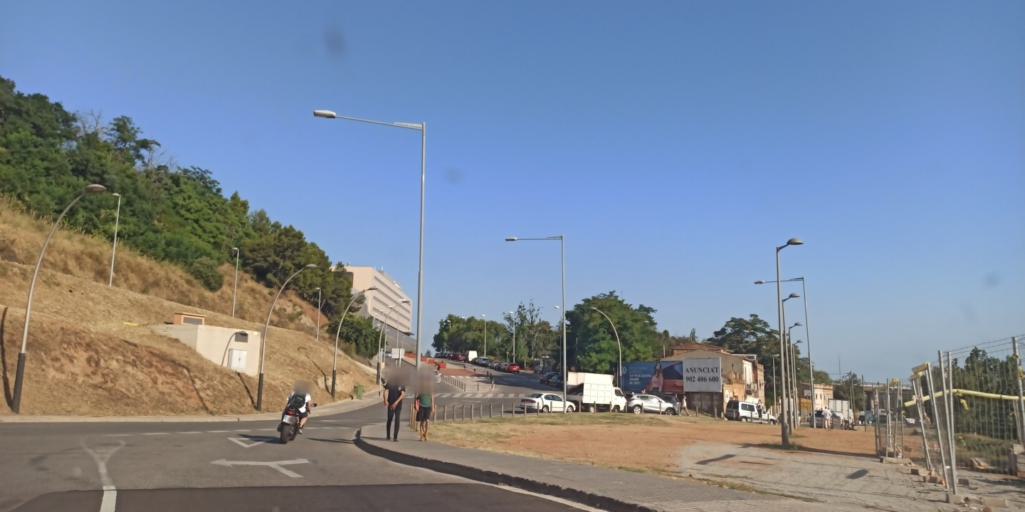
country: ES
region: Catalonia
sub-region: Provincia de Barcelona
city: Llefia
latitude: 41.4398
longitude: 2.2103
